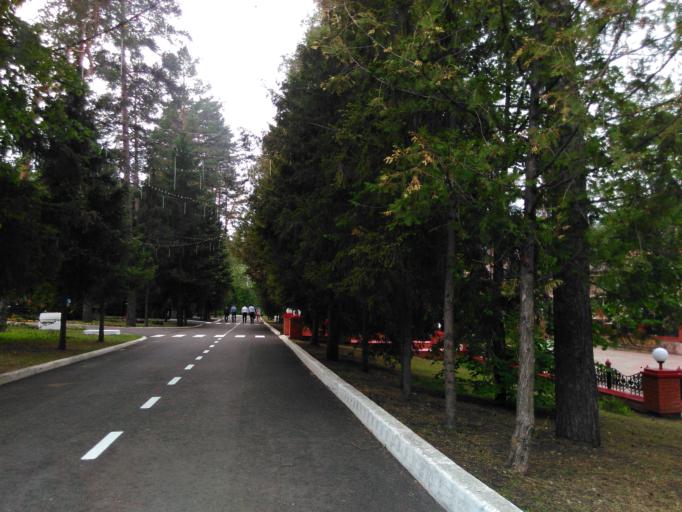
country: RU
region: Tatarstan
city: Al'met'yevsk
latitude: 54.9524
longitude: 52.2660
